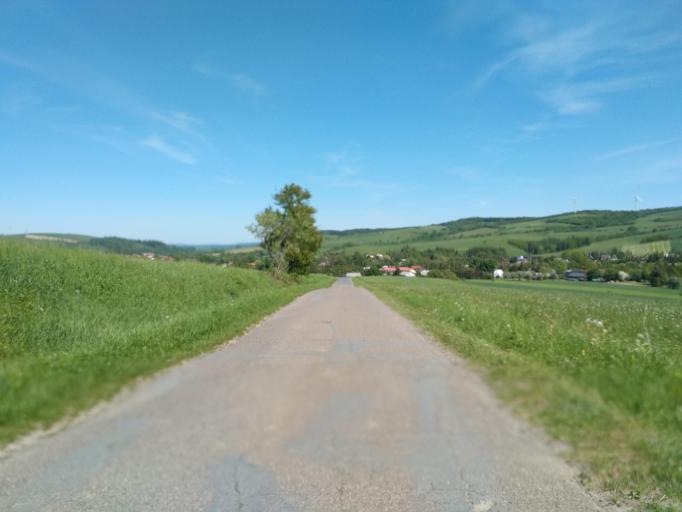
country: PL
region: Subcarpathian Voivodeship
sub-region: Powiat sanocki
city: Bukowsko
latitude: 49.4942
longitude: 22.0266
